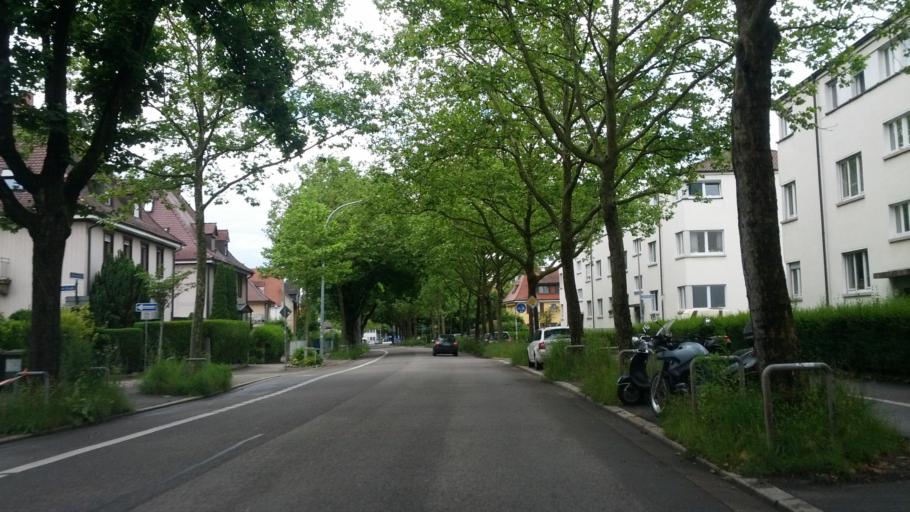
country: DE
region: Baden-Wuerttemberg
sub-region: Freiburg Region
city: Freiburg
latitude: 47.9888
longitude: 7.8799
